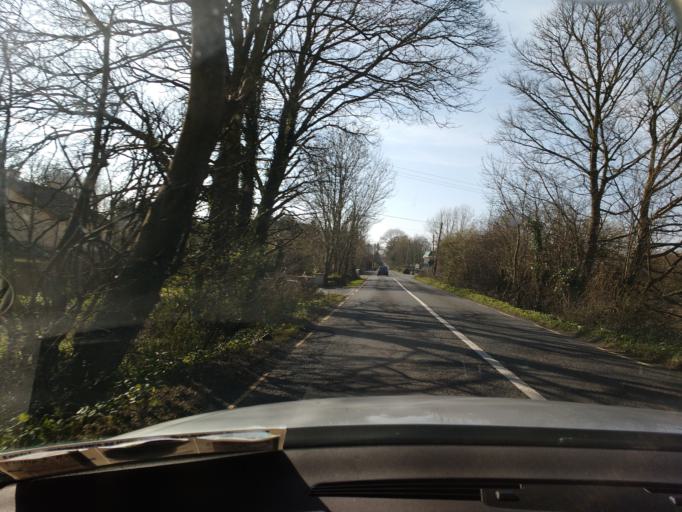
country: IE
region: Munster
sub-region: County Limerick
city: Castleconnell
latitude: 52.6807
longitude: -8.4982
